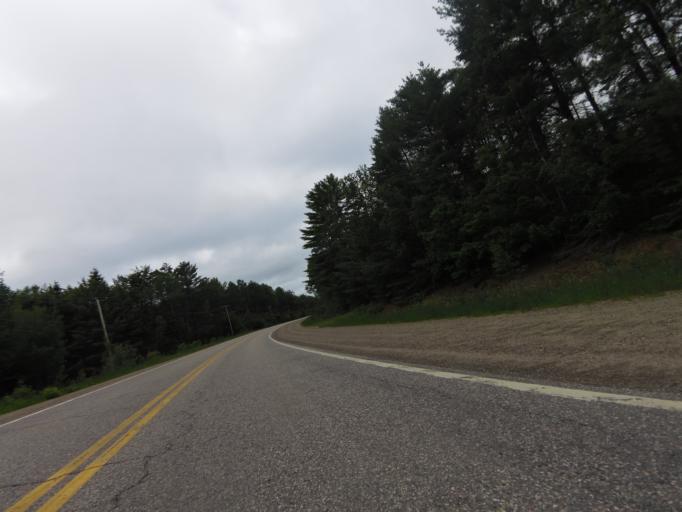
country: CA
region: Quebec
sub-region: Outaouais
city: Shawville
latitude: 45.8578
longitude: -76.4147
